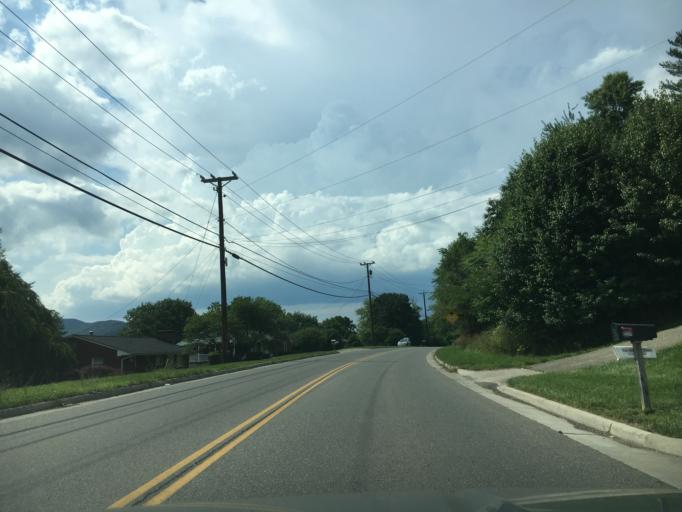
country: US
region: Virginia
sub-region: Roanoke County
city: Cave Spring
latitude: 37.2119
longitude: -80.0133
